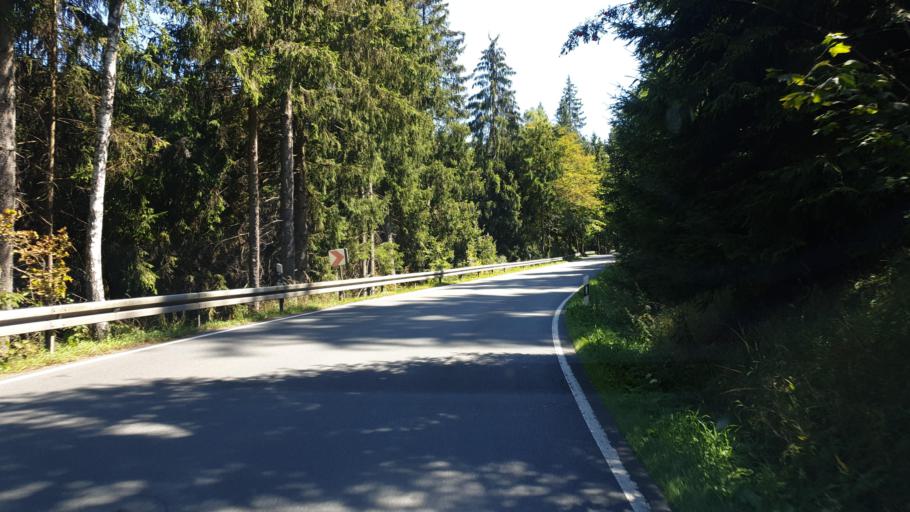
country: DE
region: Saxony
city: Sosa
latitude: 50.5141
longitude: 12.6365
